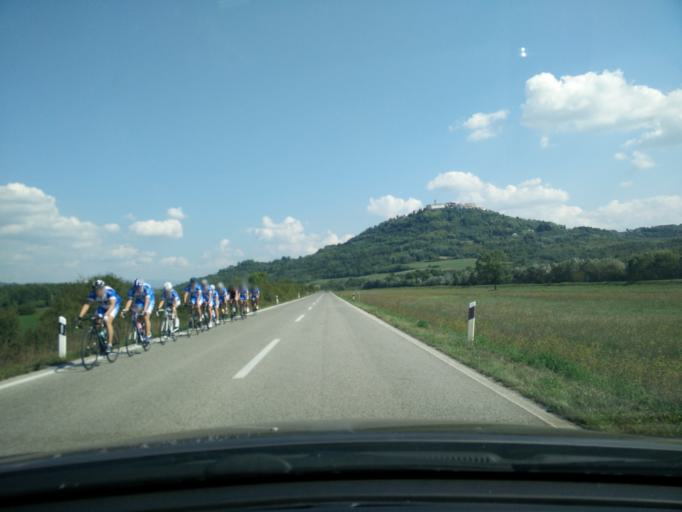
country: HR
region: Istarska
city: Karojba
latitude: 45.3450
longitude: 13.8068
